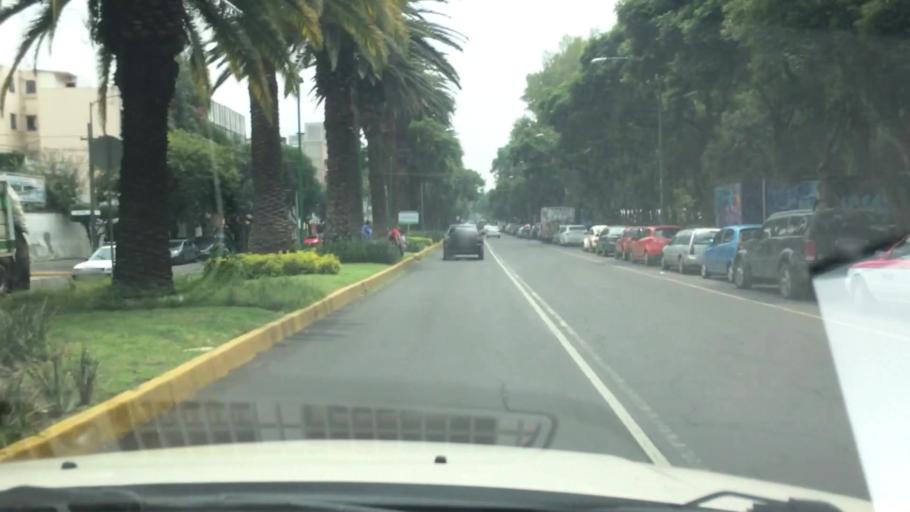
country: MX
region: Mexico City
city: Colonia del Valle
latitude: 19.3729
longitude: -99.1545
